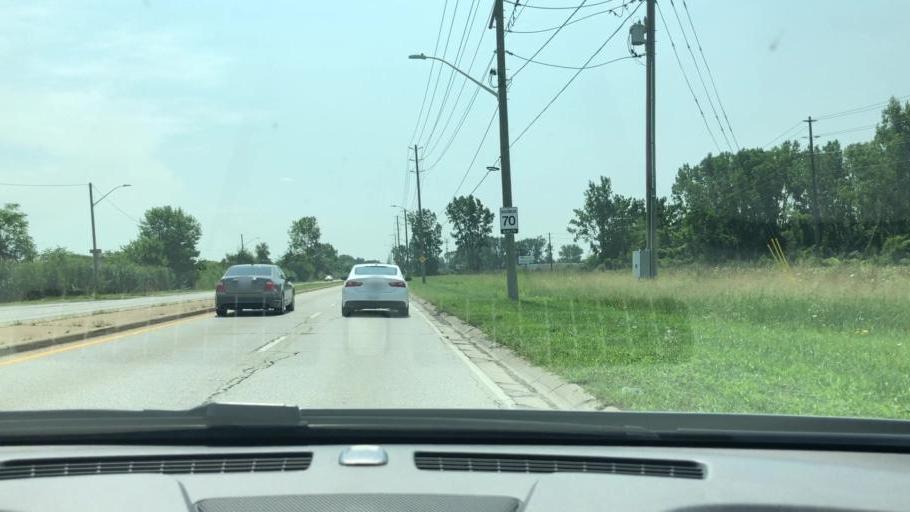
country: US
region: Michigan
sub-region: Wayne County
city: River Rouge
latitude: 42.2567
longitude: -83.0873
